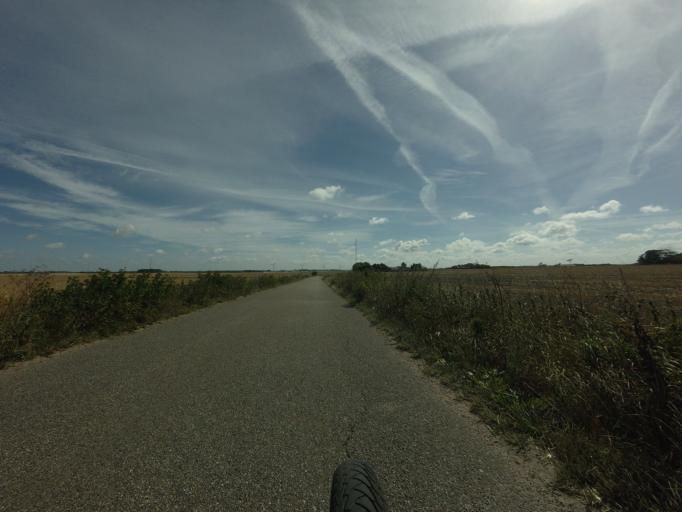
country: DK
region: North Denmark
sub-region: Hjorring Kommune
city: Vra
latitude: 57.3426
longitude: 9.7913
